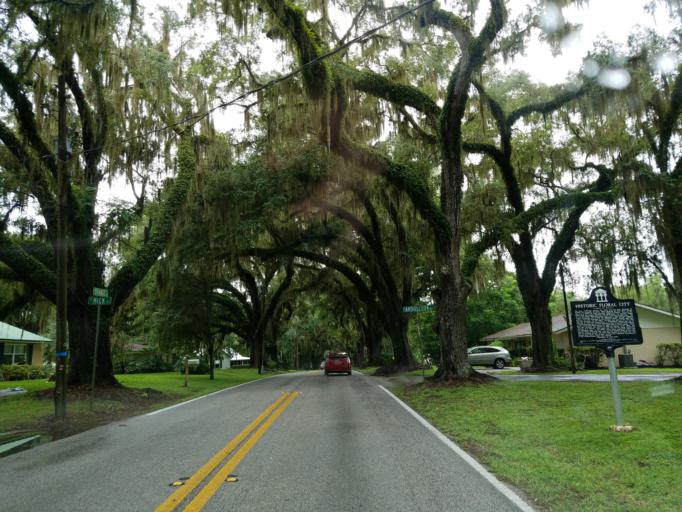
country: US
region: Florida
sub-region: Citrus County
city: Floral City
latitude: 28.7502
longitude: -82.2876
